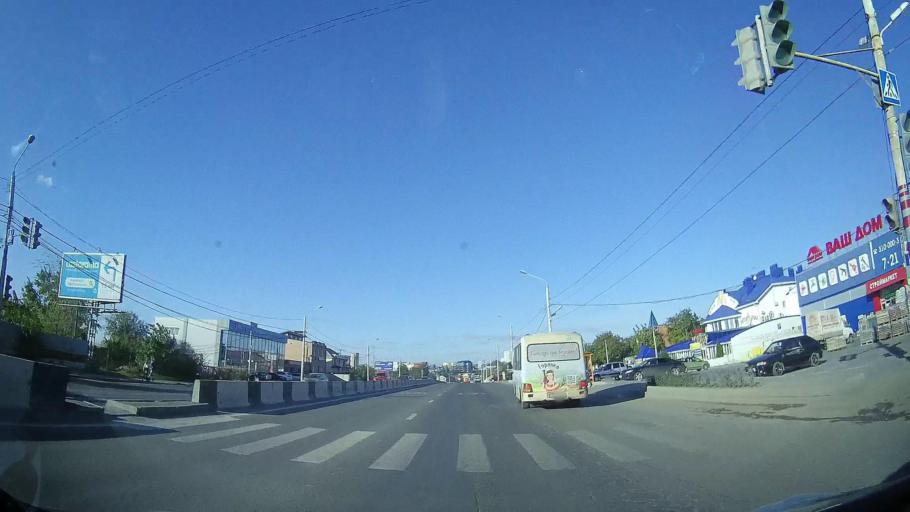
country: RU
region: Rostov
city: Kalinin
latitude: 47.2167
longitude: 39.6135
